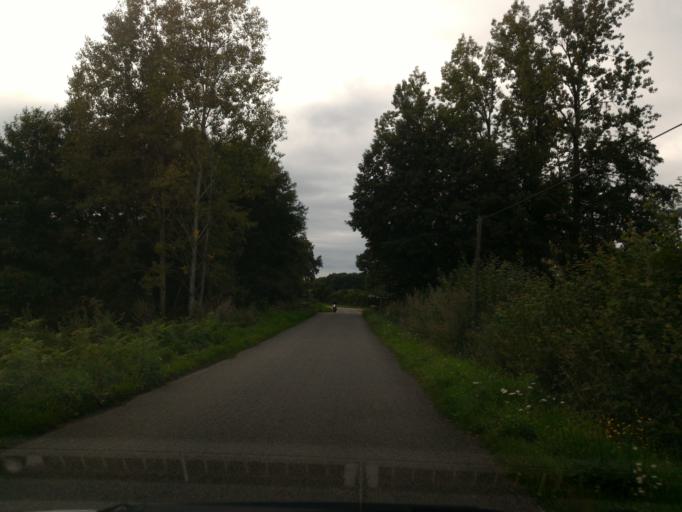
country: FR
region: Poitou-Charentes
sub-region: Departement de la Charente
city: Brigueuil
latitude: 45.9320
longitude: 0.8233
